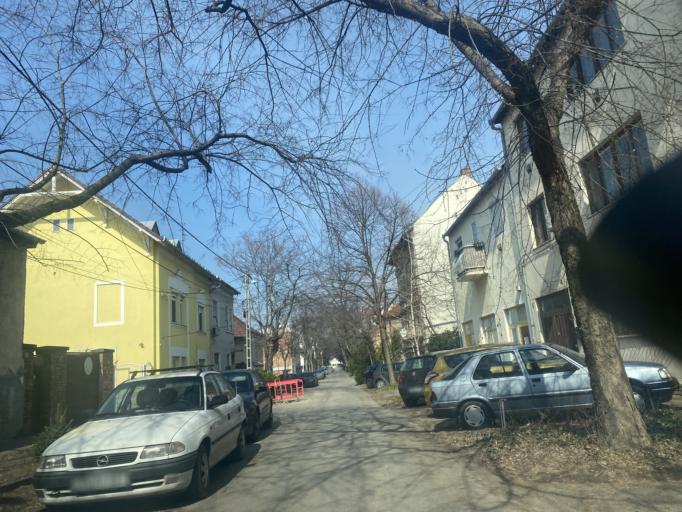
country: HU
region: Csongrad
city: Szeged
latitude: 46.2620
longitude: 20.1531
